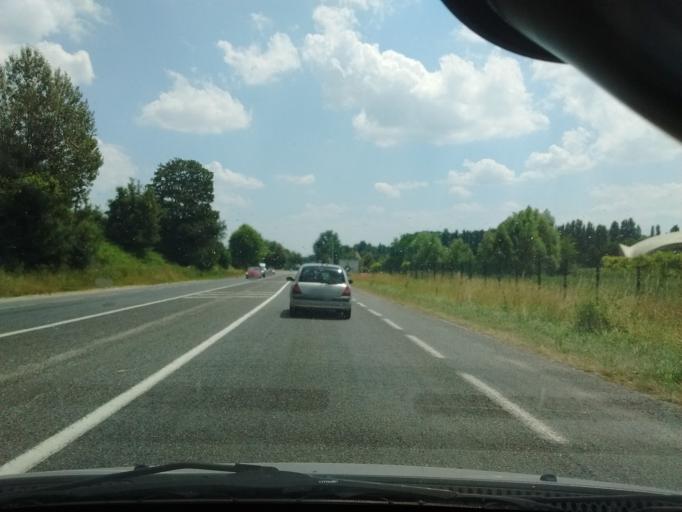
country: FR
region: Ile-de-France
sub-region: Departement de Seine-et-Marne
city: Ponthierry
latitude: 48.5372
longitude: 2.5243
